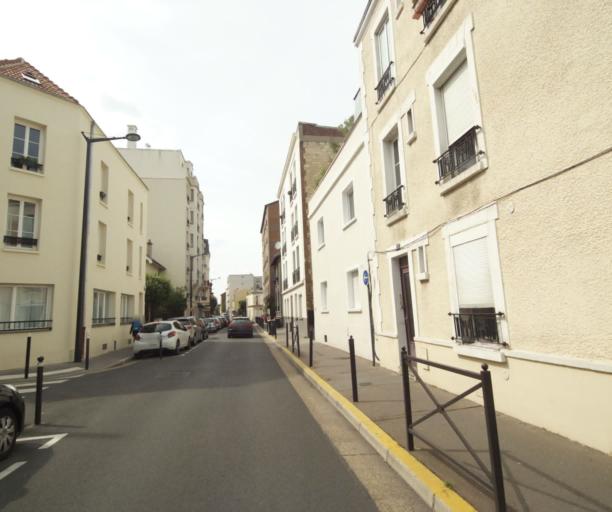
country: FR
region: Ile-de-France
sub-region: Departement des Hauts-de-Seine
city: Bois-Colombes
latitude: 48.9185
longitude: 2.2748
